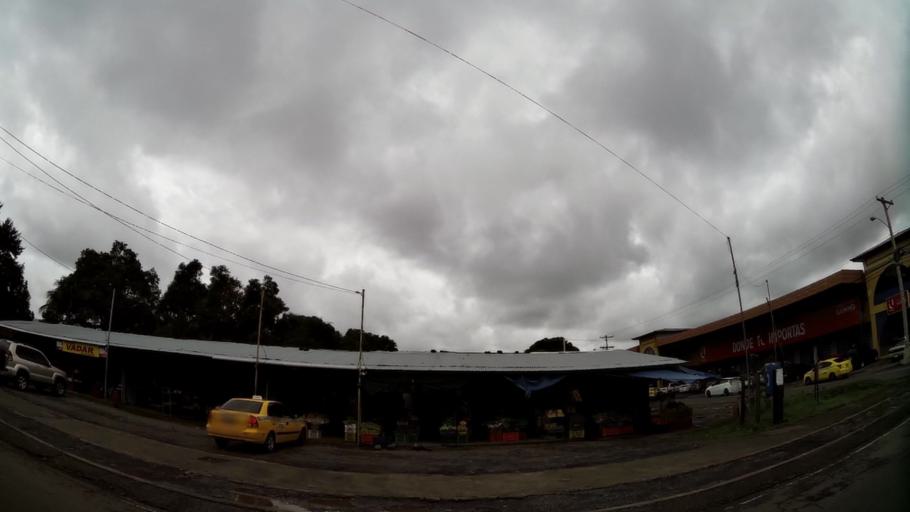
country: PA
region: Chiriqui
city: David
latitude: 8.4267
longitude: -82.4308
